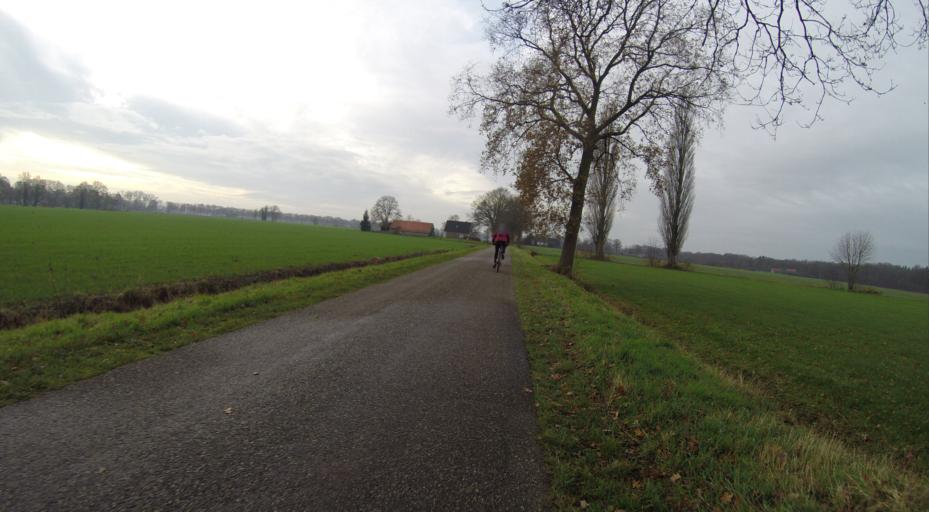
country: NL
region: Gelderland
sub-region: Gemeente Lochem
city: Lochem
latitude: 52.1451
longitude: 6.4021
